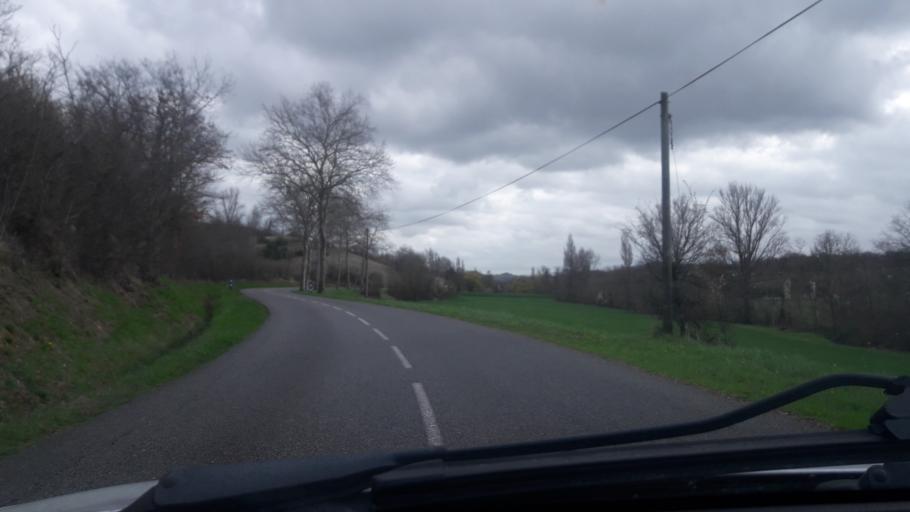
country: FR
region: Midi-Pyrenees
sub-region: Departement de la Haute-Garonne
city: Rieux-Volvestre
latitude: 43.2542
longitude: 1.2472
